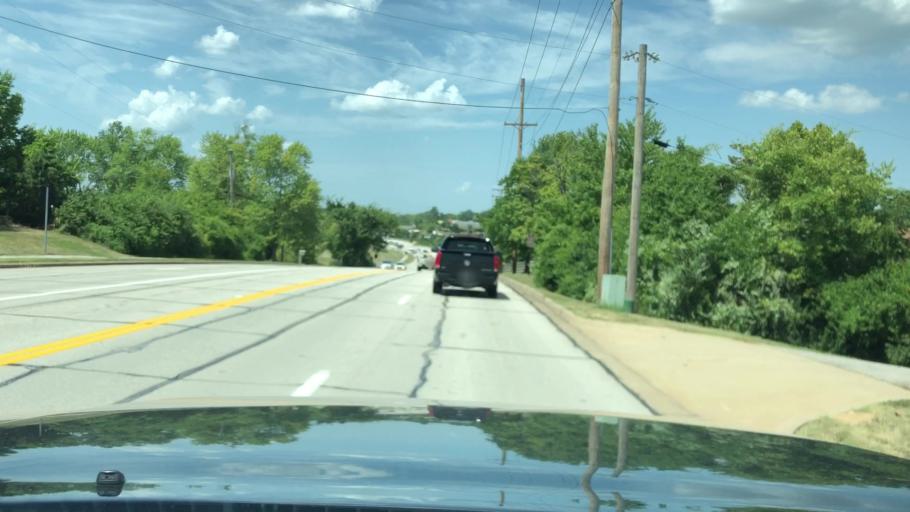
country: US
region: Missouri
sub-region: Saint Charles County
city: O'Fallon
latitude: 38.7918
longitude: -90.6915
